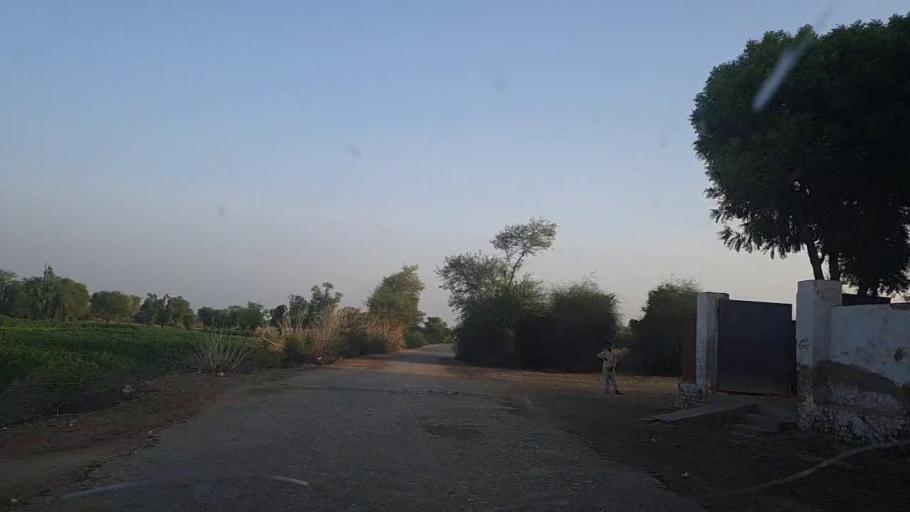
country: PK
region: Sindh
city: Khanpur
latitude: 27.6237
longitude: 69.4448
